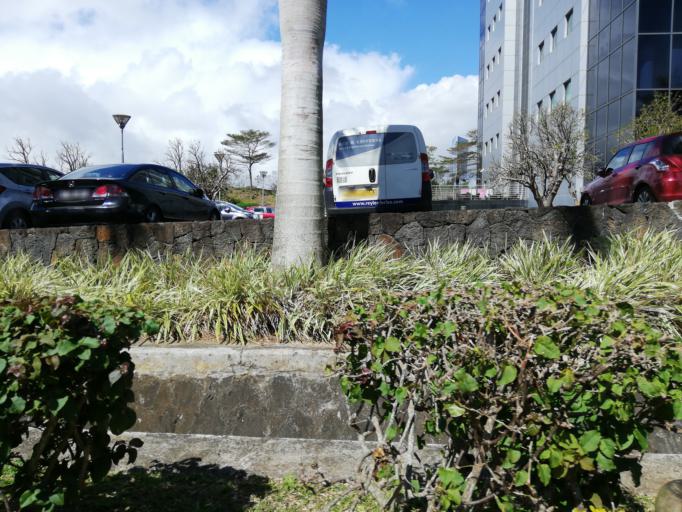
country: MU
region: Plaines Wilhems
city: Ebene
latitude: -20.2427
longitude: 57.4962
